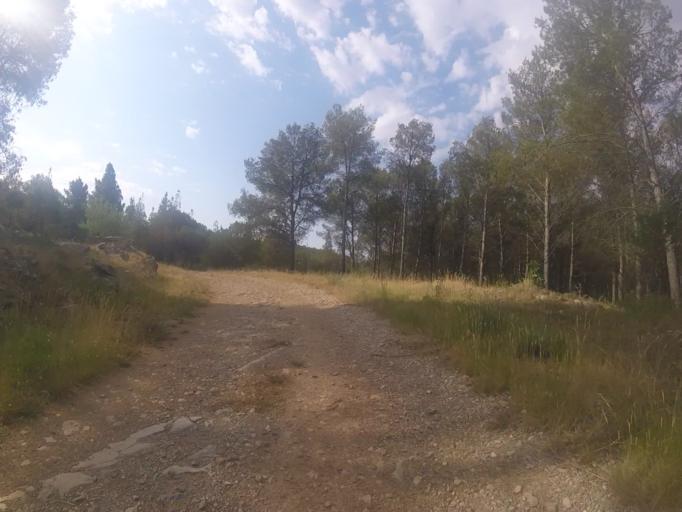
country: ES
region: Valencia
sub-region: Provincia de Castello
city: Cervera del Maestre
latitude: 40.3976
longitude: 0.2057
